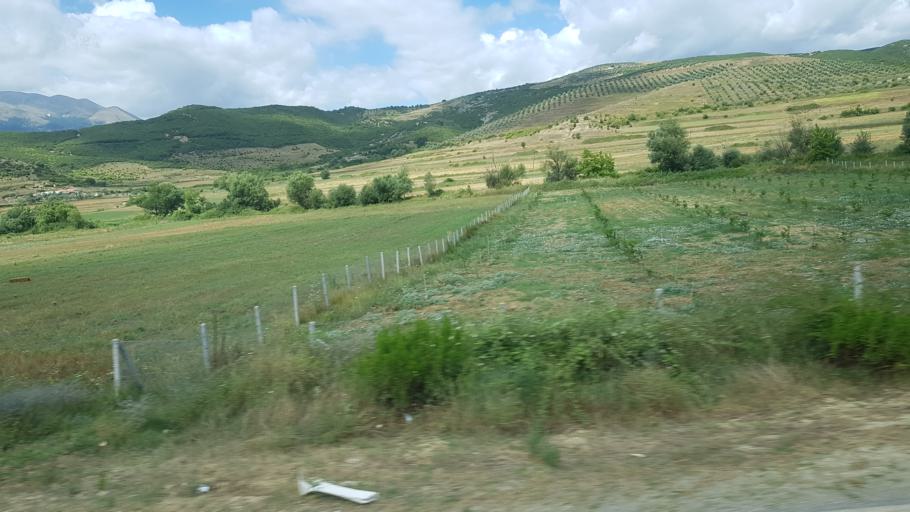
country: AL
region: Gjirokaster
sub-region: Rrethi i Tepelenes
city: Krahes
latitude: 40.4205
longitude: 19.8579
